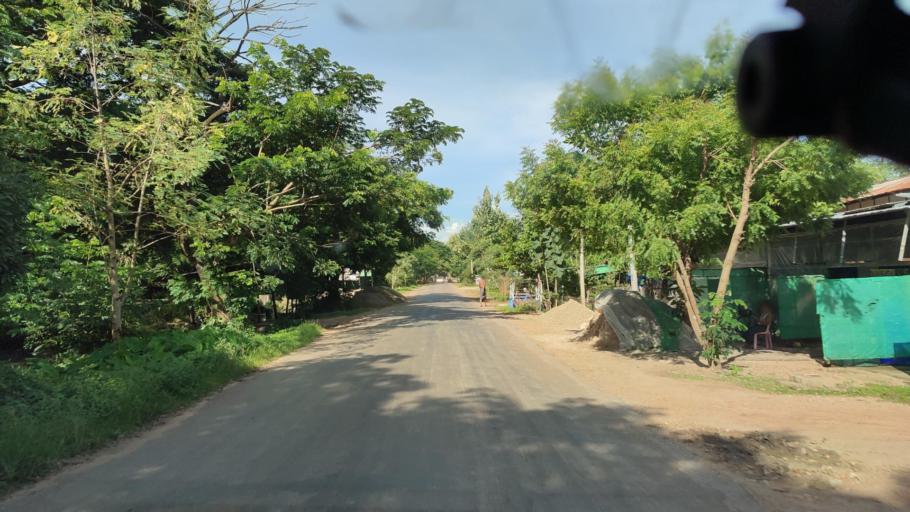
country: MM
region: Bago
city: Paungde
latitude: 18.3380
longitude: 95.6190
